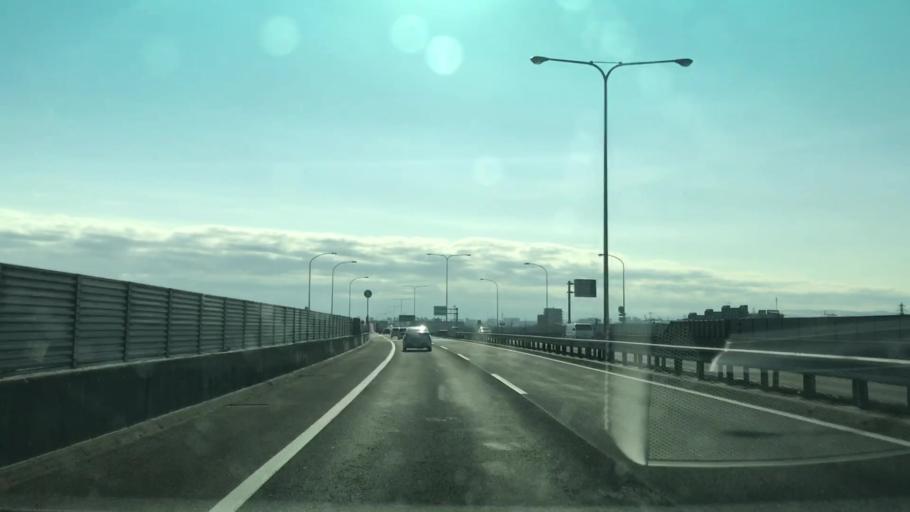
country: JP
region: Hokkaido
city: Sapporo
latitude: 43.0589
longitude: 141.4257
